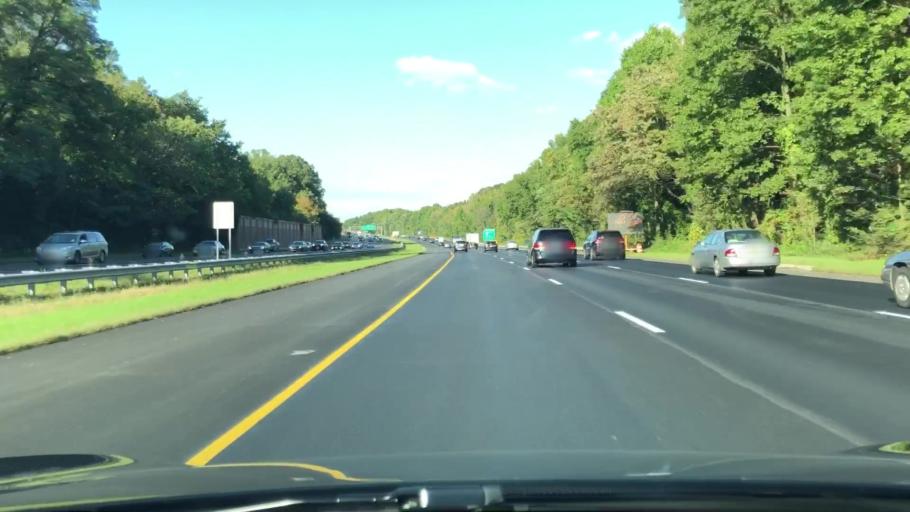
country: US
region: New Jersey
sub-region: Camden County
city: Springdale
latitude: 39.8986
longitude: -74.9900
